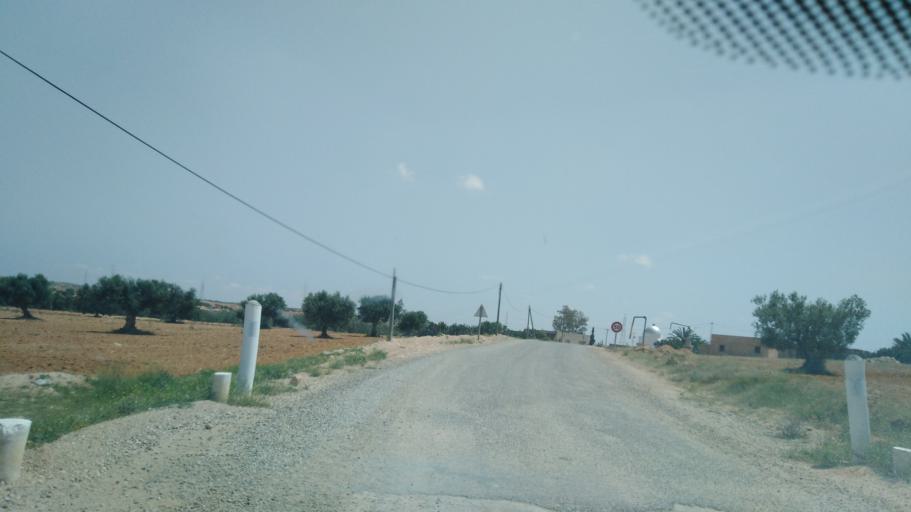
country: TN
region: Safaqis
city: Sfax
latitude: 34.7498
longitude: 10.5674
